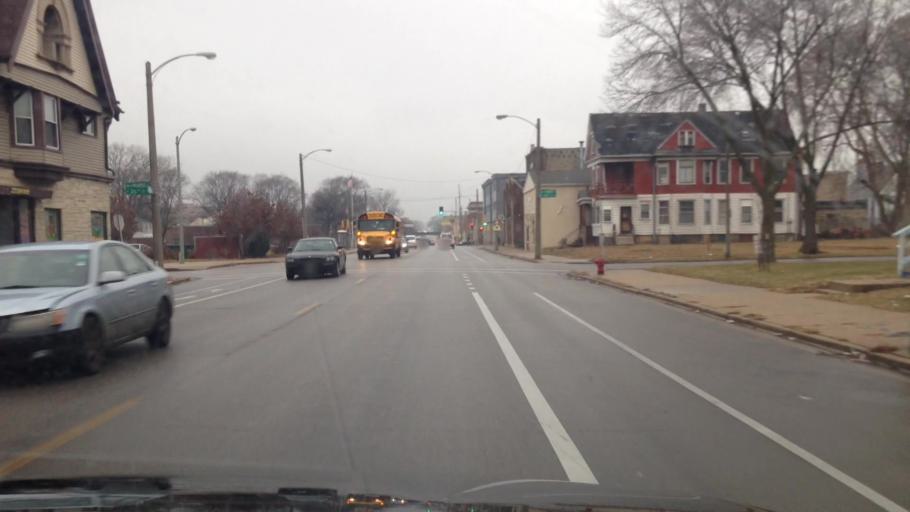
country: US
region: Wisconsin
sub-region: Milwaukee County
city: Milwaukee
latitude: 43.0679
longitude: -87.9456
